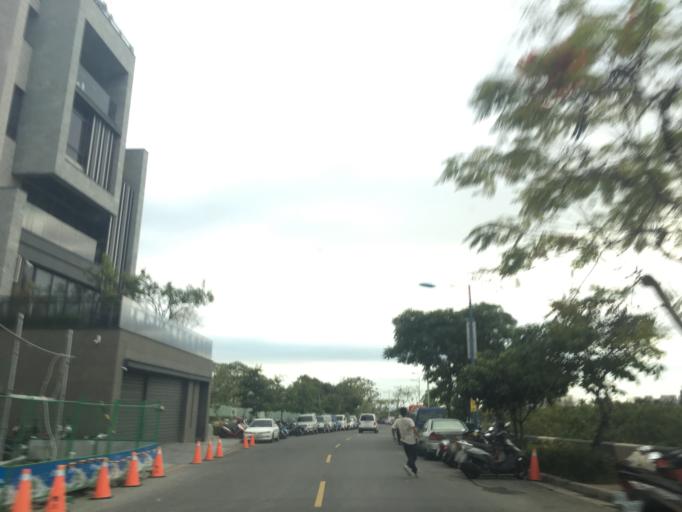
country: TW
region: Taiwan
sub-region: Taichung City
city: Taichung
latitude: 24.1576
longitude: 120.7291
